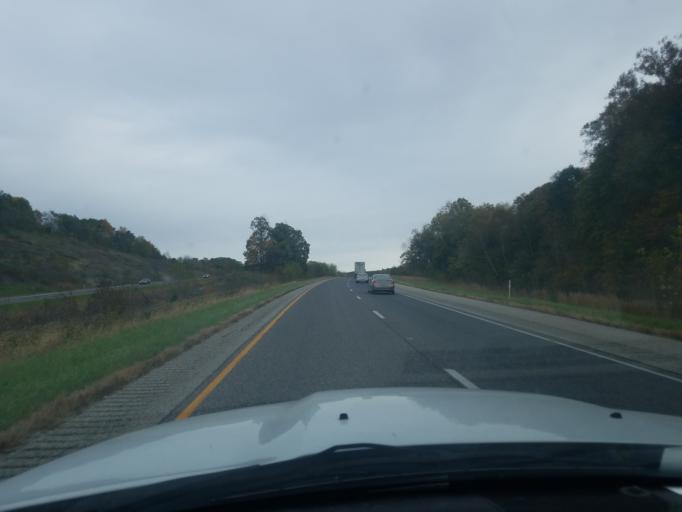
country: US
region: Indiana
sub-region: Dubois County
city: Ferdinand
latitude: 38.2115
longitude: -86.7694
